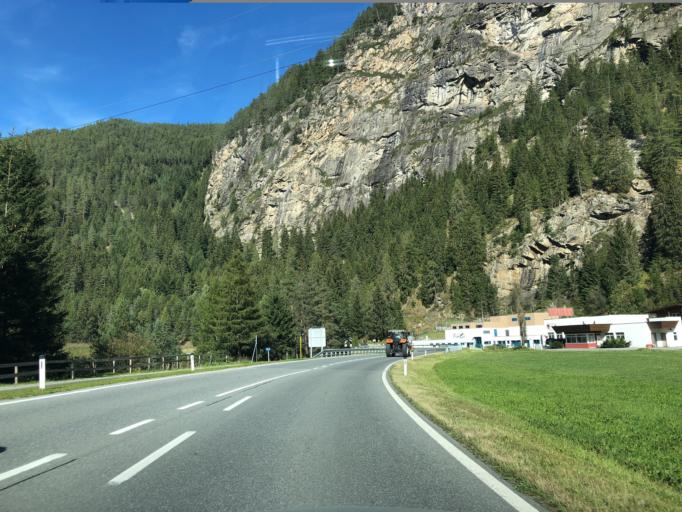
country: AT
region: Tyrol
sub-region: Politischer Bezirk Imst
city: Umhausen
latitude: 47.1044
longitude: 10.9524
